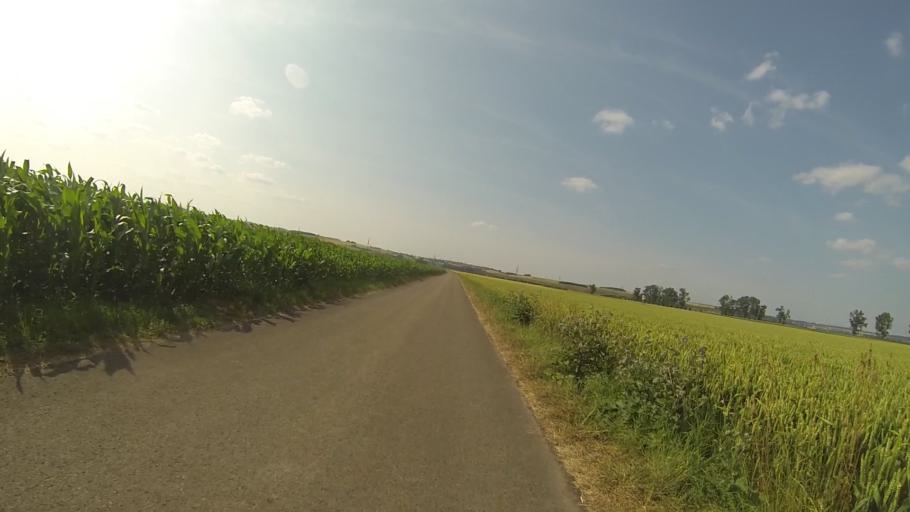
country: DE
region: Baden-Wuerttemberg
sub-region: Tuebingen Region
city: Asselfingen
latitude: 48.5021
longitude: 10.2149
